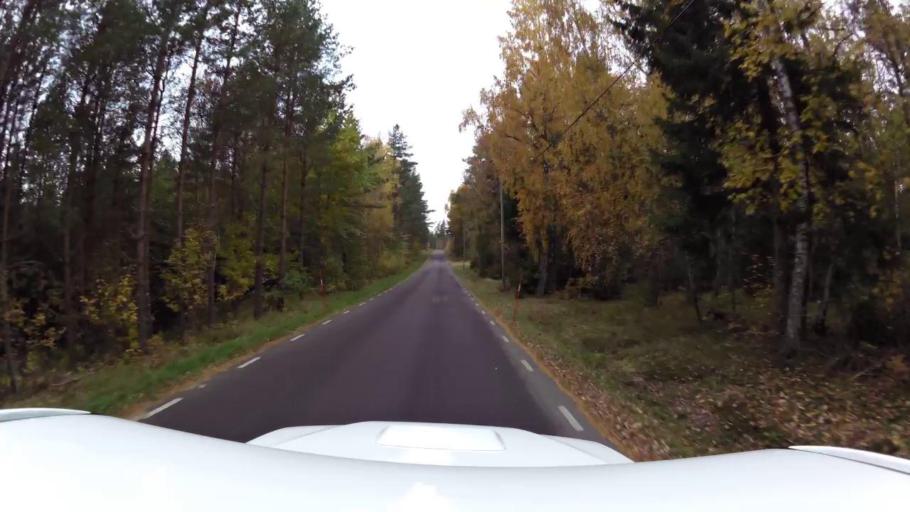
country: SE
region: OEstergoetland
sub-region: Linkopings Kommun
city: Ljungsbro
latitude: 58.5558
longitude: 15.4027
